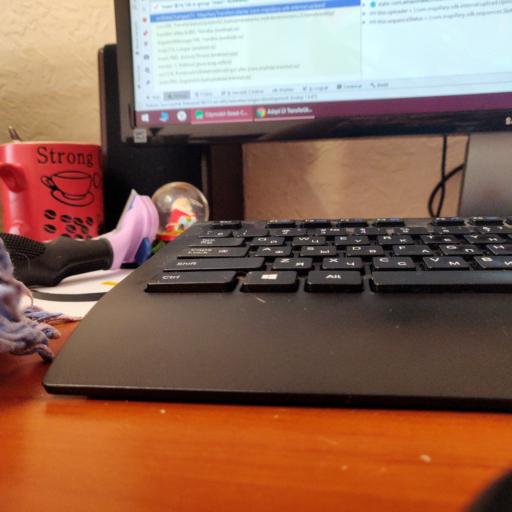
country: FI
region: Haeme
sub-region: Forssa
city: Humppila
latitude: 60.8837
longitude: 23.4322
